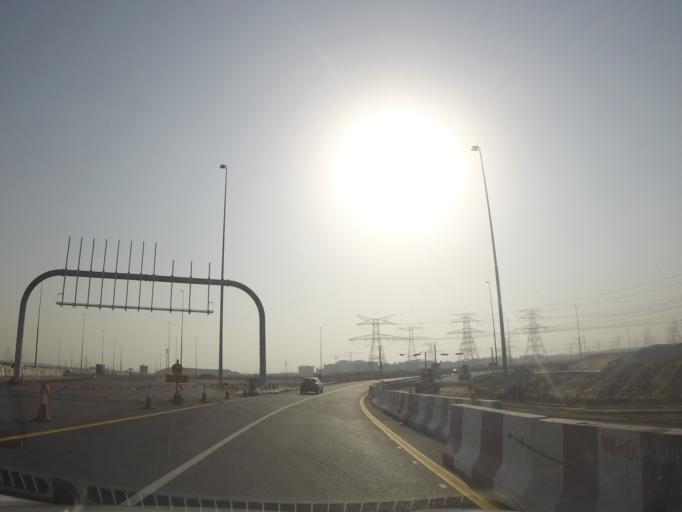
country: AE
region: Dubai
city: Dubai
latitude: 25.0339
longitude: 55.1649
